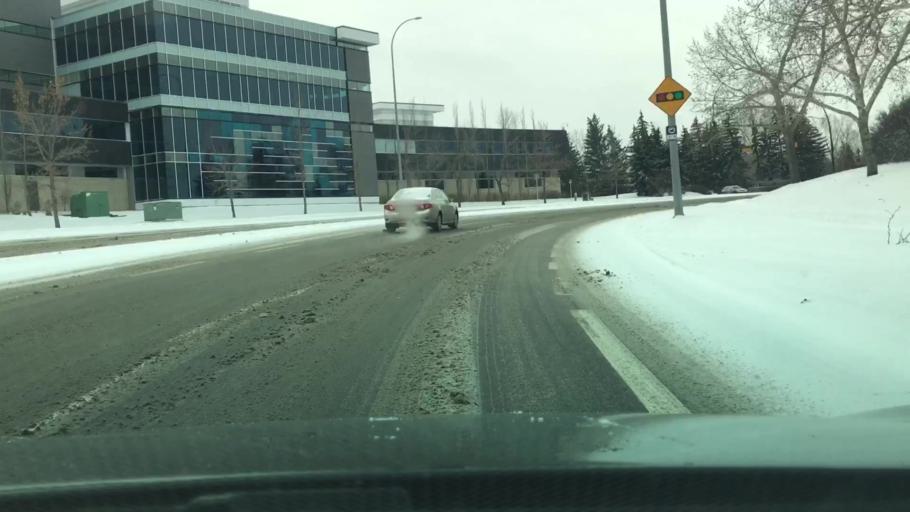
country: CA
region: Alberta
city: Calgary
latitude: 51.0875
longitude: -114.1370
